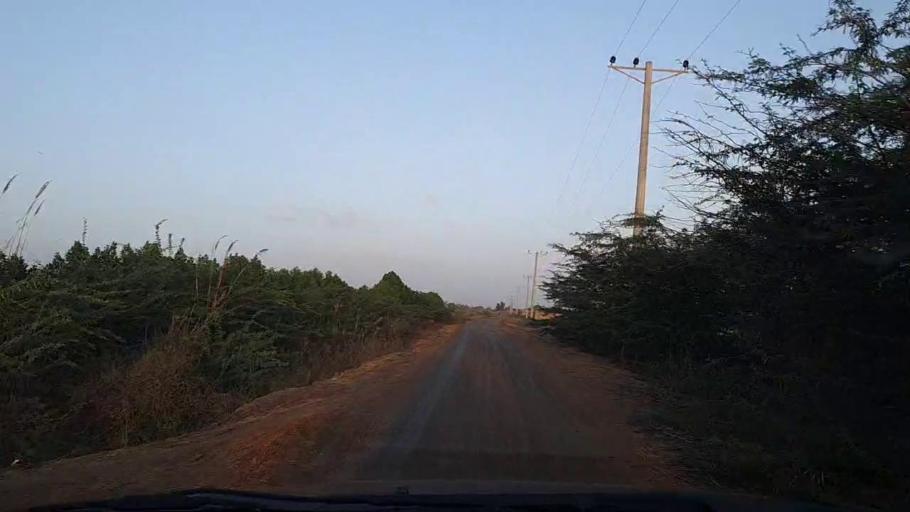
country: PK
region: Sindh
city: Keti Bandar
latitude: 24.1627
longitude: 67.6105
